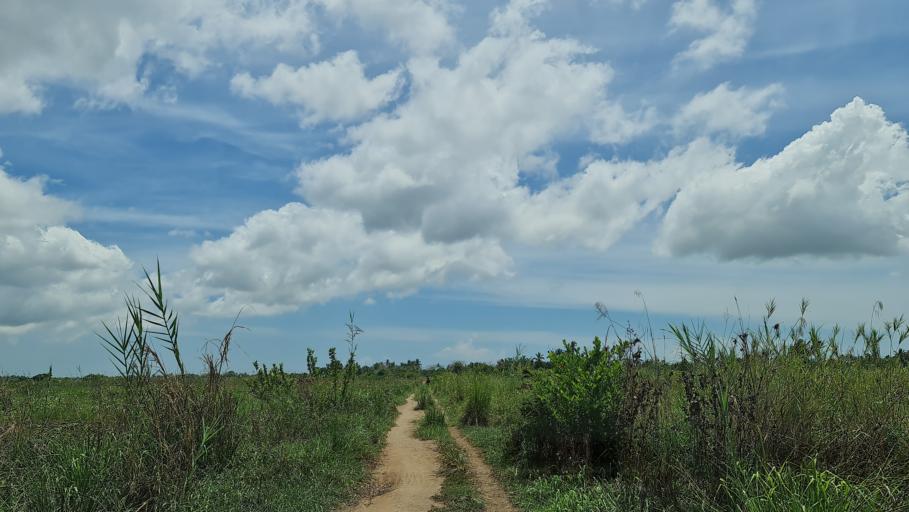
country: MZ
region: Zambezia
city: Quelimane
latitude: -17.5822
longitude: 37.3764
